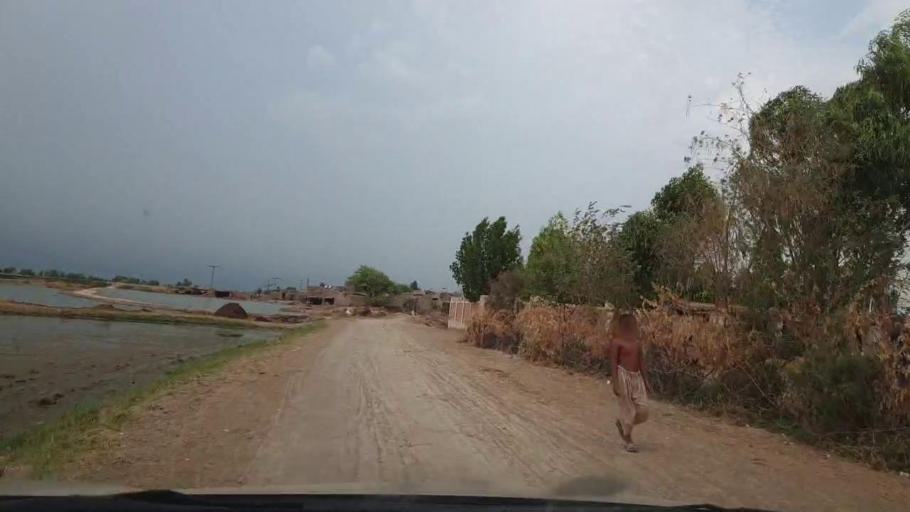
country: PK
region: Sindh
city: Ratodero
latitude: 27.8201
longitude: 68.3174
